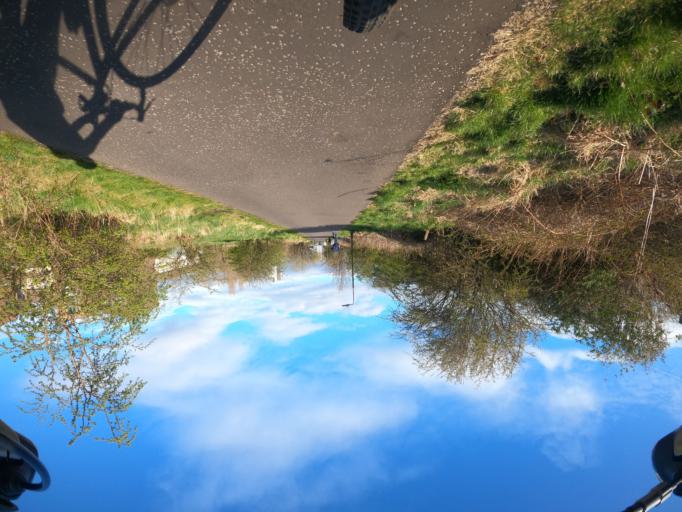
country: GB
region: Scotland
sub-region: Edinburgh
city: Edinburgh
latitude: 55.9650
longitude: -3.2415
